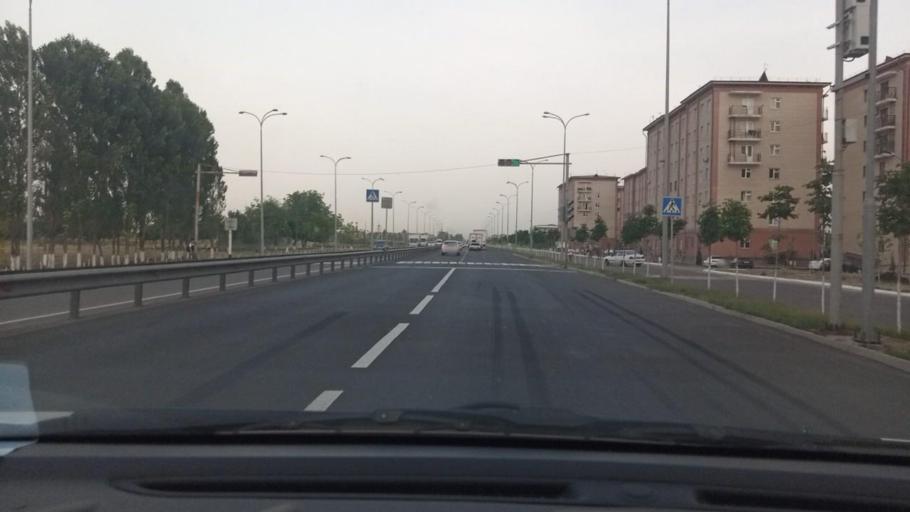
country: UZ
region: Toshkent
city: Ohangaron
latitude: 40.9142
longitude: 69.6095
